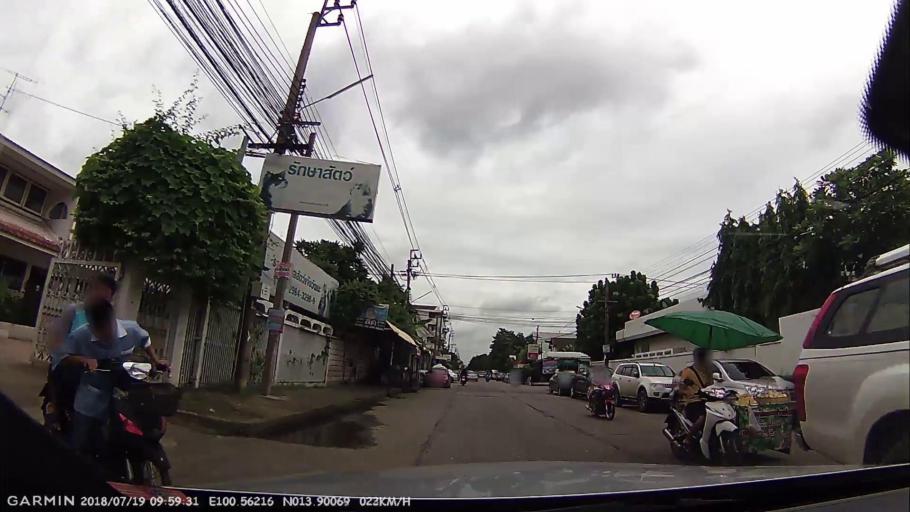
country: TH
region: Bangkok
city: Lak Si
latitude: 13.9007
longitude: 100.5622
